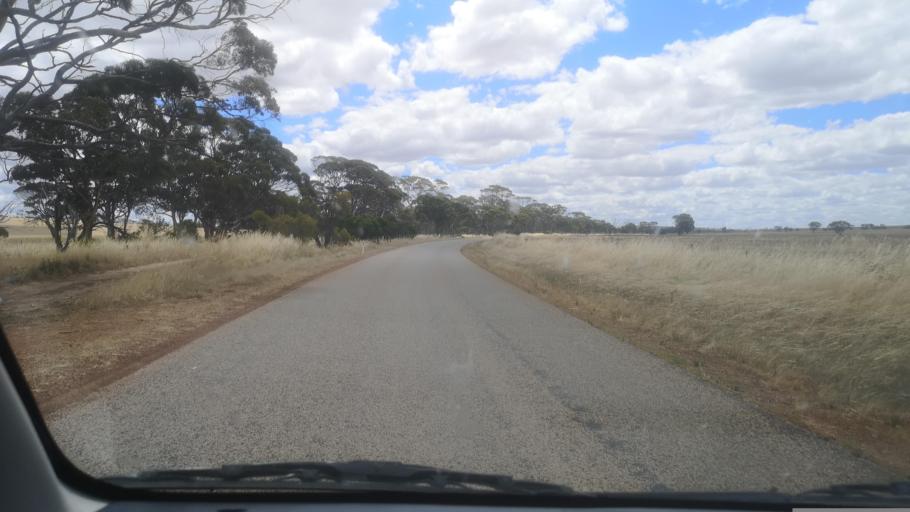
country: AU
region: Western Australia
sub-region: Cunderdin
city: Cunderdin
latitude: -32.0509
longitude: 117.4155
